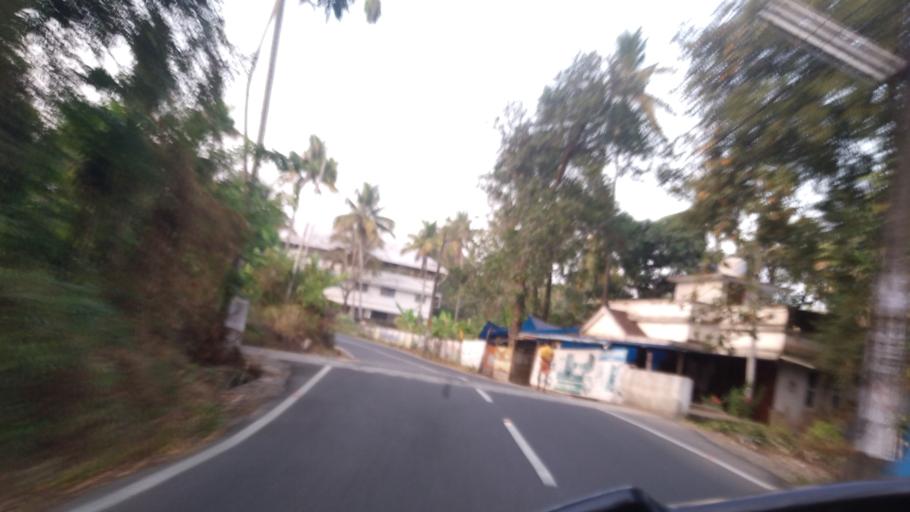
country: IN
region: Kerala
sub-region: Ernakulam
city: Elur
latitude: 10.1119
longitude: 76.2439
